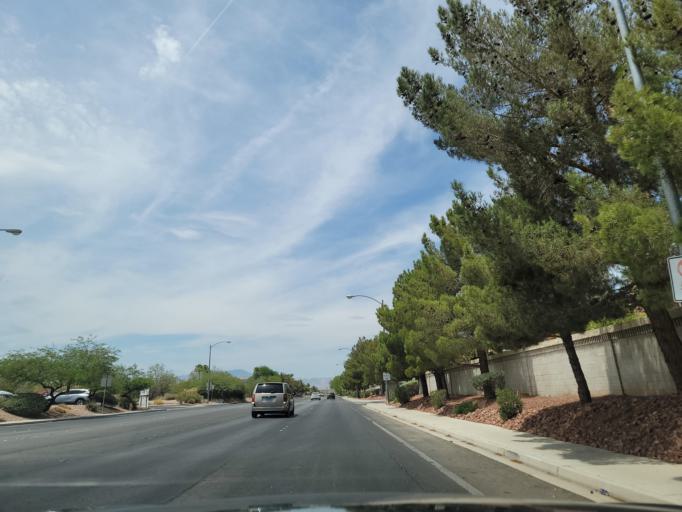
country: US
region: Nevada
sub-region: Clark County
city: Whitney
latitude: 36.0207
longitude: -115.1408
